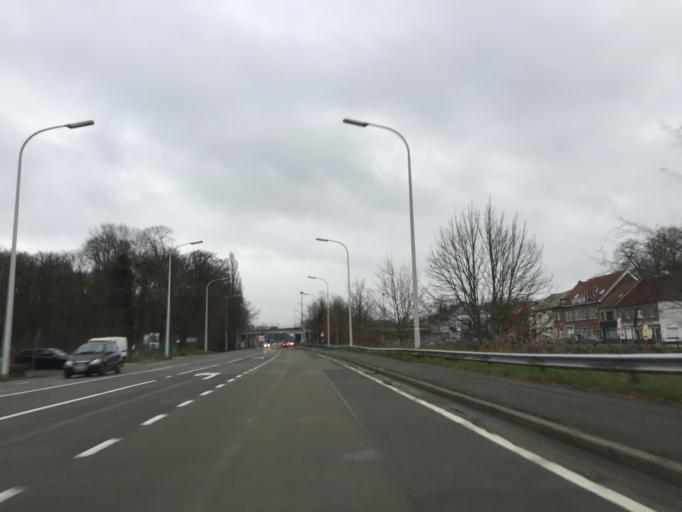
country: BE
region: Flanders
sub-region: Provincie Oost-Vlaanderen
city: Evergem
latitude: 51.0795
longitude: 3.6749
